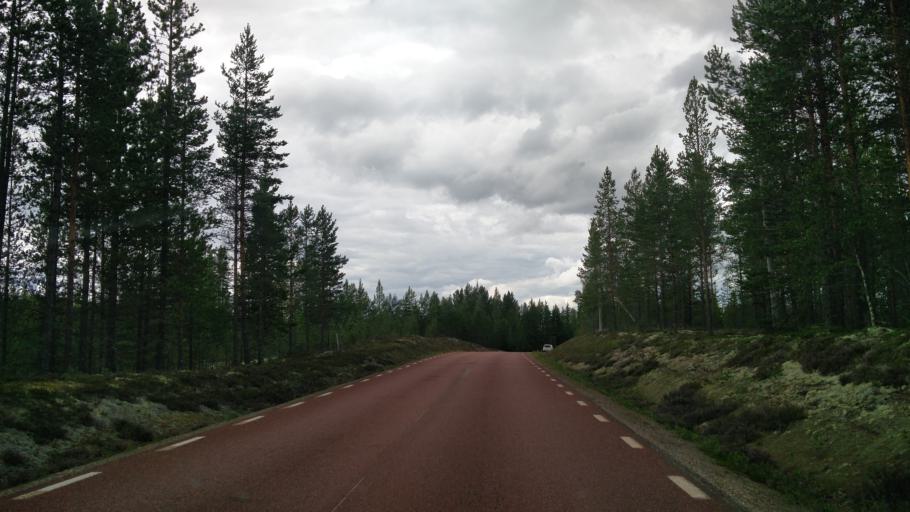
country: NO
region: Hedmark
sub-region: Trysil
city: Innbygda
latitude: 61.1459
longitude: 12.8045
